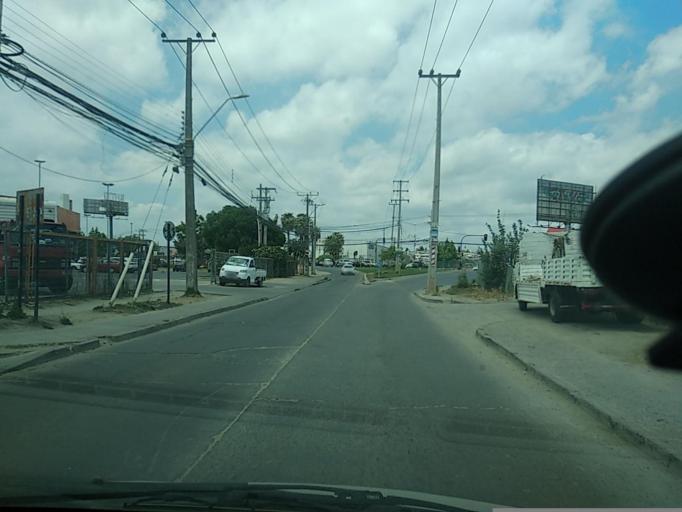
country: CL
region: Valparaiso
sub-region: Provincia de Marga Marga
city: Quilpue
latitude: -33.0433
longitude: -71.4193
